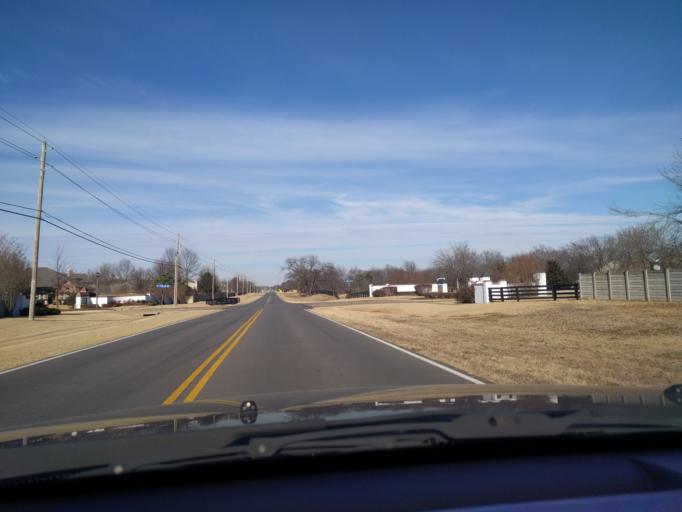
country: US
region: Oklahoma
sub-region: Tulsa County
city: Broken Arrow
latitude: 36.0490
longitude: -95.7080
